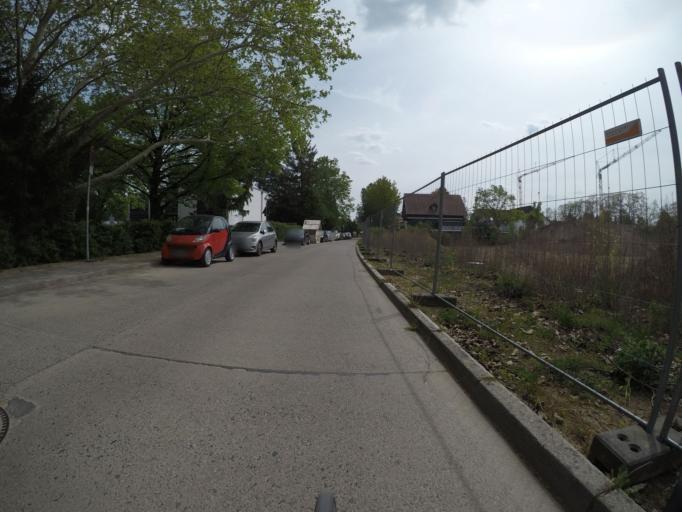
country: DE
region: Berlin
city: Lichtenrade
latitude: 52.3933
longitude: 13.3950
